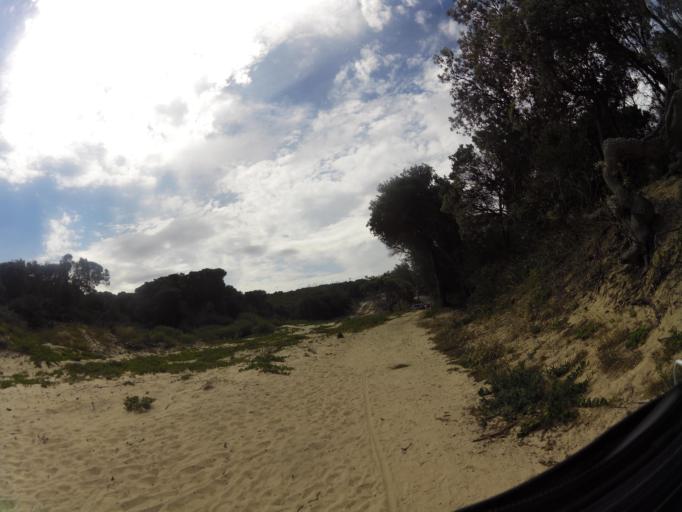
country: AU
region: Victoria
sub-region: East Gippsland
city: Lakes Entrance
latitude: -37.8054
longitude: 148.6346
